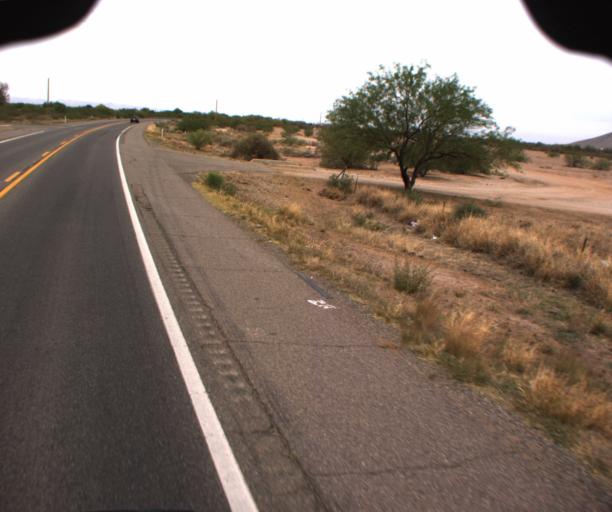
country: US
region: Arizona
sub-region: Pinal County
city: Sacaton
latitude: 33.1240
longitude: -111.7445
